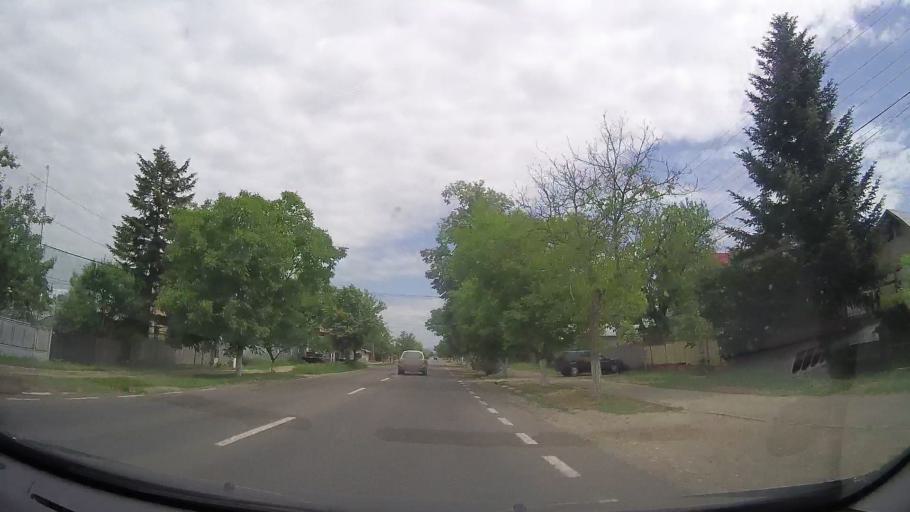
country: RO
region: Prahova
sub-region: Comuna Lipanesti
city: Lipanesti
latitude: 45.0499
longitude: 26.0194
